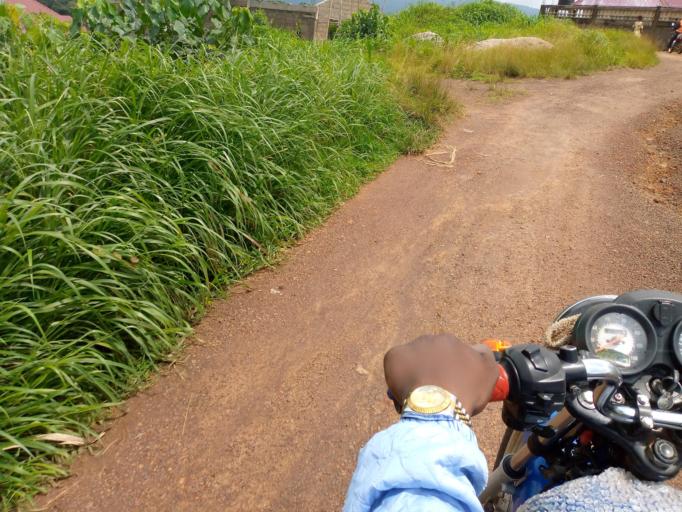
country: SL
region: Eastern Province
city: Kenema
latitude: 7.8786
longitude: -11.1667
